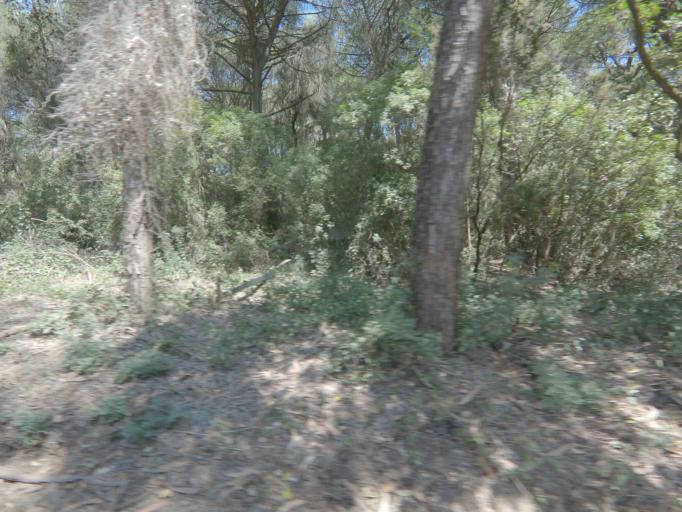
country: PT
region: Setubal
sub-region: Setubal
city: Setubal
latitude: 38.5110
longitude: -8.9289
